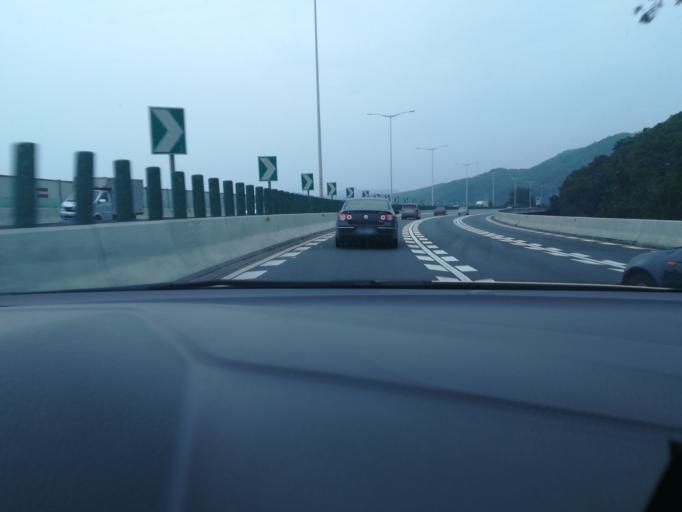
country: CN
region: Guangdong
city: Longdong
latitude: 23.2411
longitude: 113.3506
